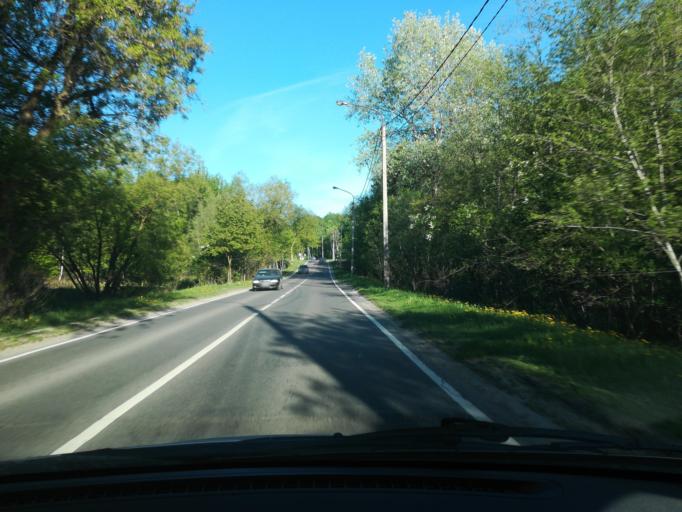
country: LT
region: Vilnius County
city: Rasos
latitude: 54.6671
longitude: 25.3215
